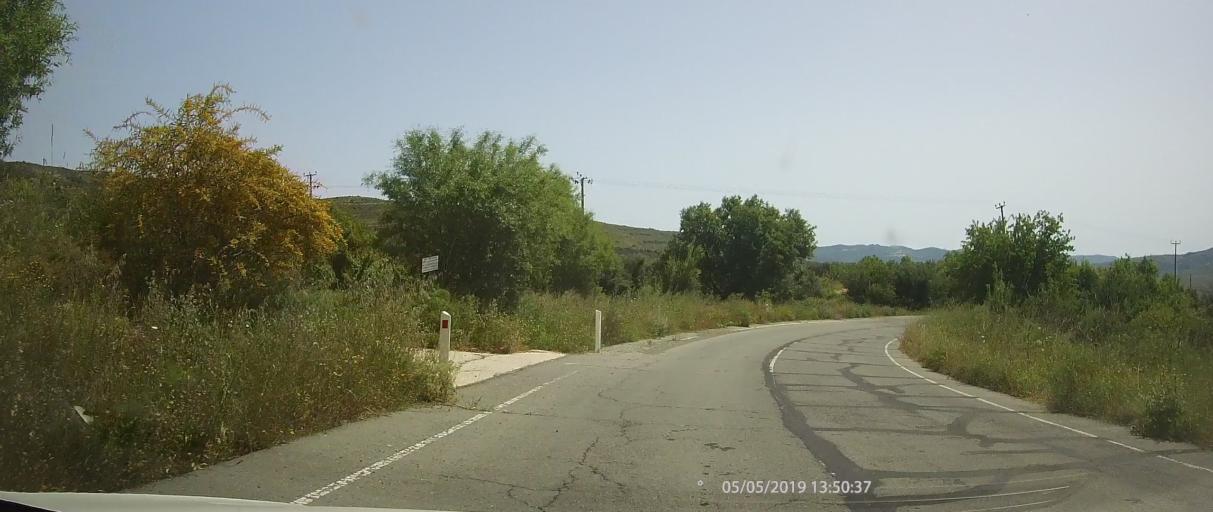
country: CY
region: Limassol
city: Pachna
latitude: 34.8410
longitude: 32.7378
